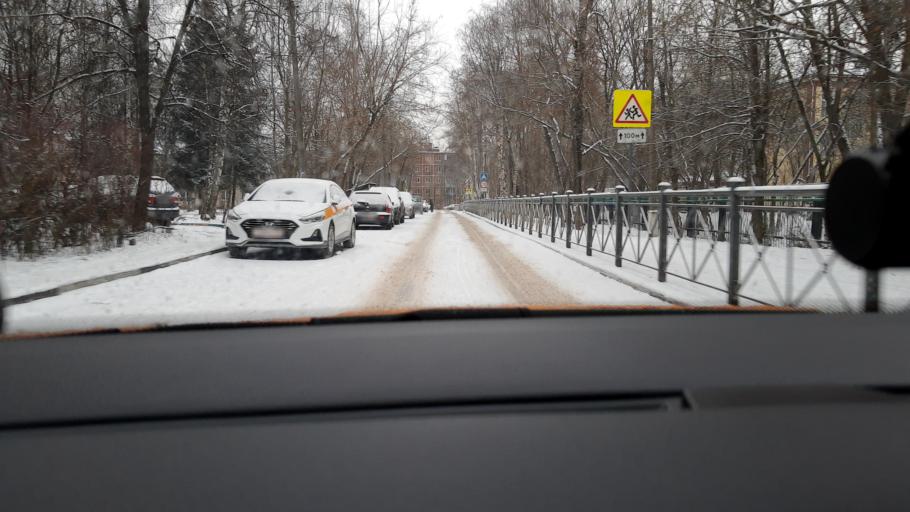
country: RU
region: Moskovskaya
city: Skhodnya
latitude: 55.9438
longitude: 37.2961
